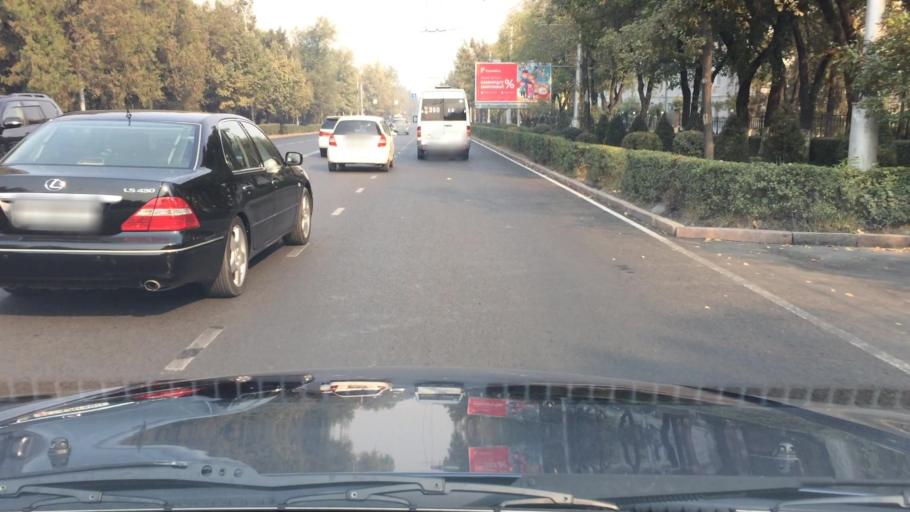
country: KG
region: Chuy
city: Bishkek
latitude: 42.8451
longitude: 74.5862
